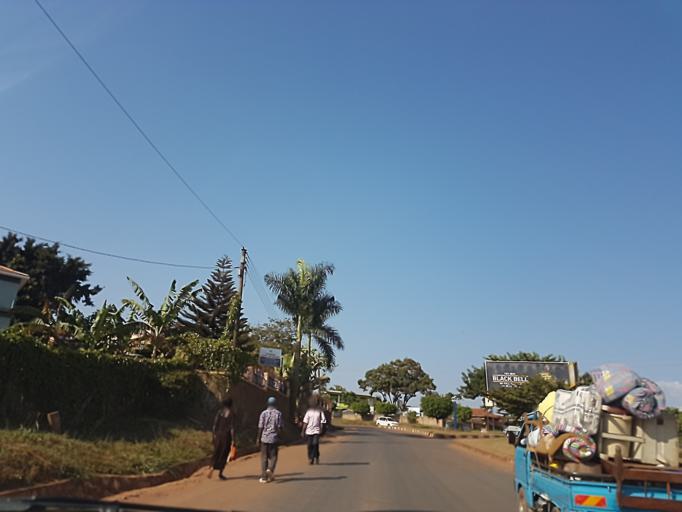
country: UG
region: Central Region
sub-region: Wakiso District
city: Kireka
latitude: 0.3455
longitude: 32.6172
